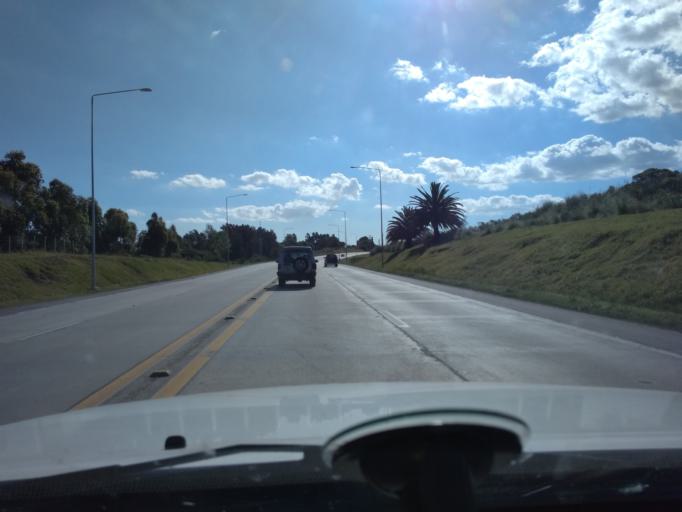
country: UY
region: Canelones
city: La Paz
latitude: -34.7825
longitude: -56.2451
